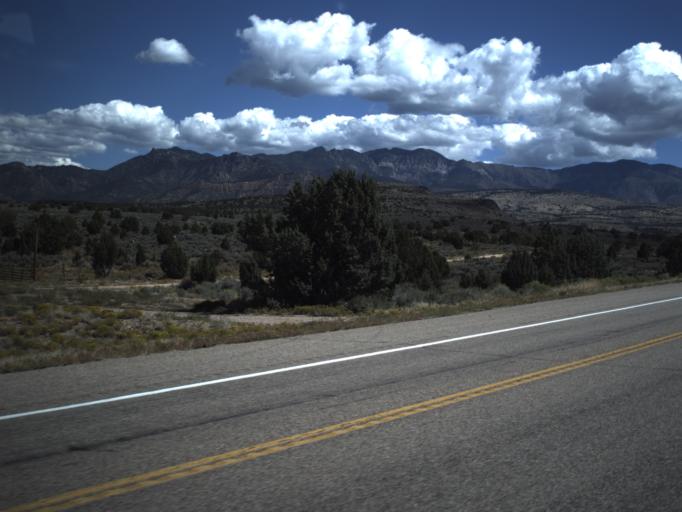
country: US
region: Utah
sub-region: Washington County
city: Ivins
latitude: 37.3203
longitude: -113.6878
